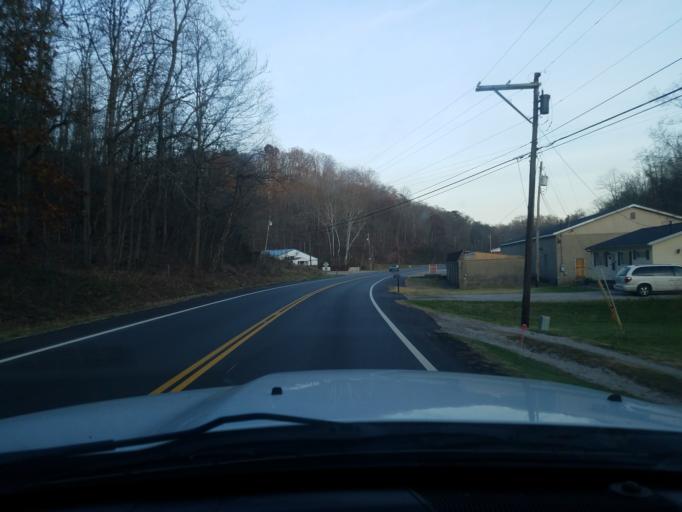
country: US
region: Ohio
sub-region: Washington County
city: Marietta
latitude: 39.4071
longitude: -81.4901
